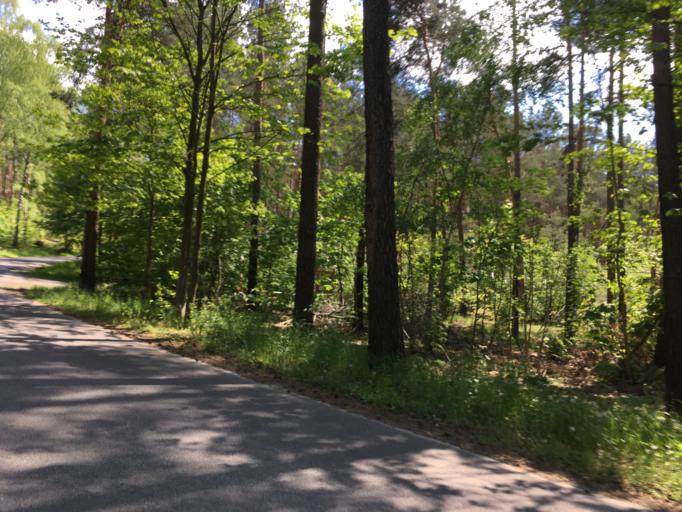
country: DE
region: Brandenburg
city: Rudnitz
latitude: 52.7101
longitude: 13.6598
